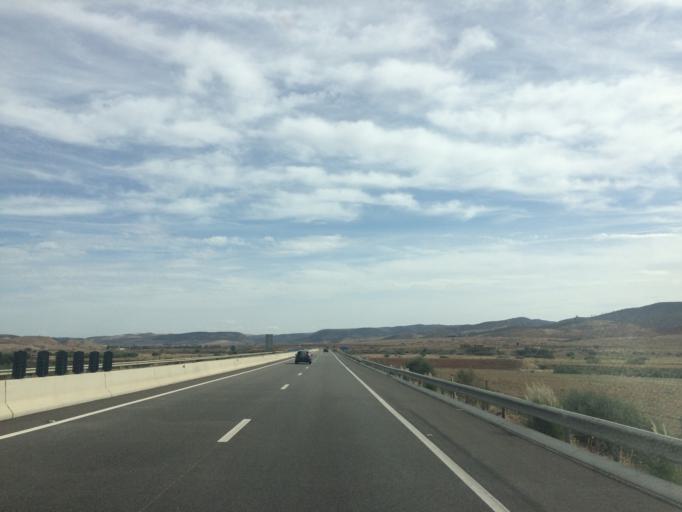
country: MA
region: Rabat-Sale-Zemmour-Zaer
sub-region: Khemisset
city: Khemisset
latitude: 33.7795
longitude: -5.9483
